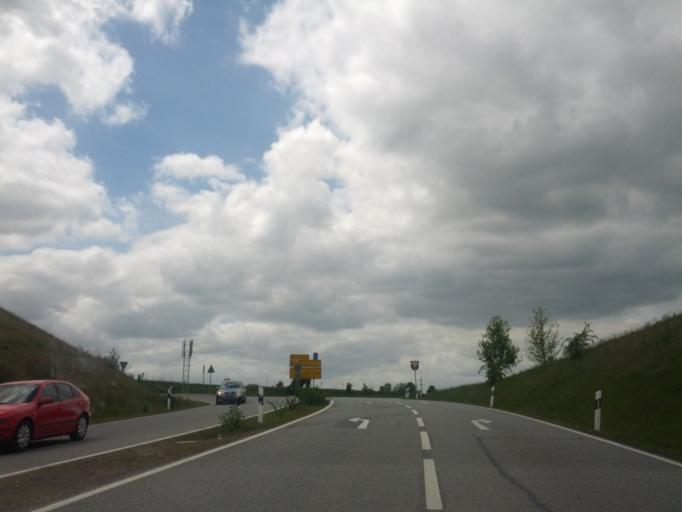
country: DE
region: Saxony
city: Dohna
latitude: 50.9738
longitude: 13.8110
